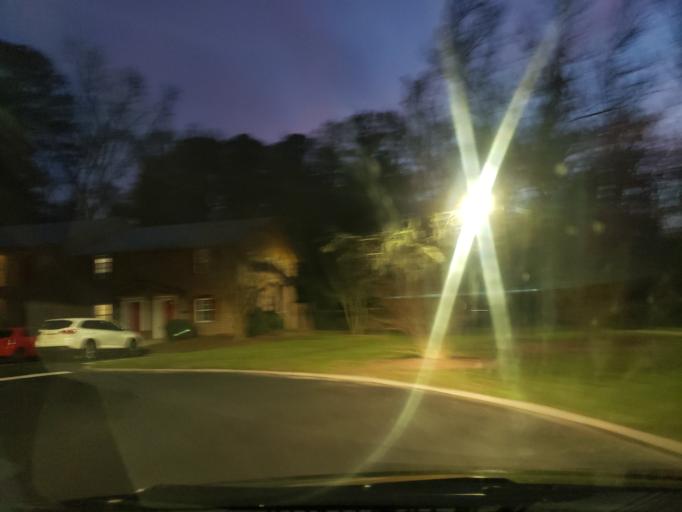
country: US
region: Georgia
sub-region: Chatham County
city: Montgomery
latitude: 31.9896
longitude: -81.1358
